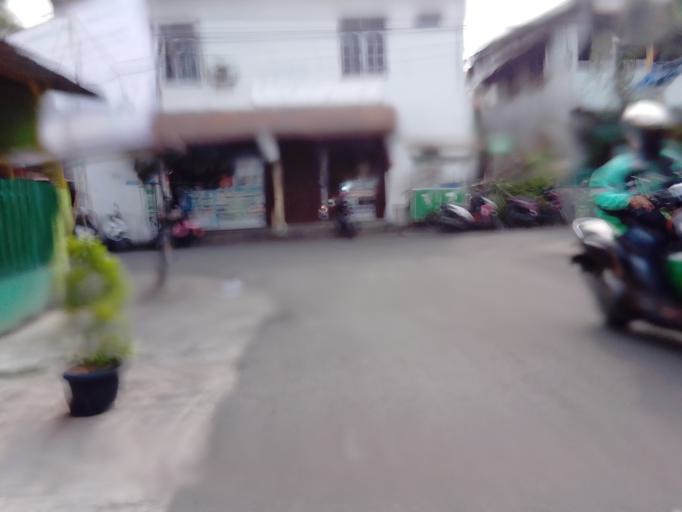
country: ID
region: Jakarta Raya
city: Jakarta
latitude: -6.1530
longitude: 106.8138
